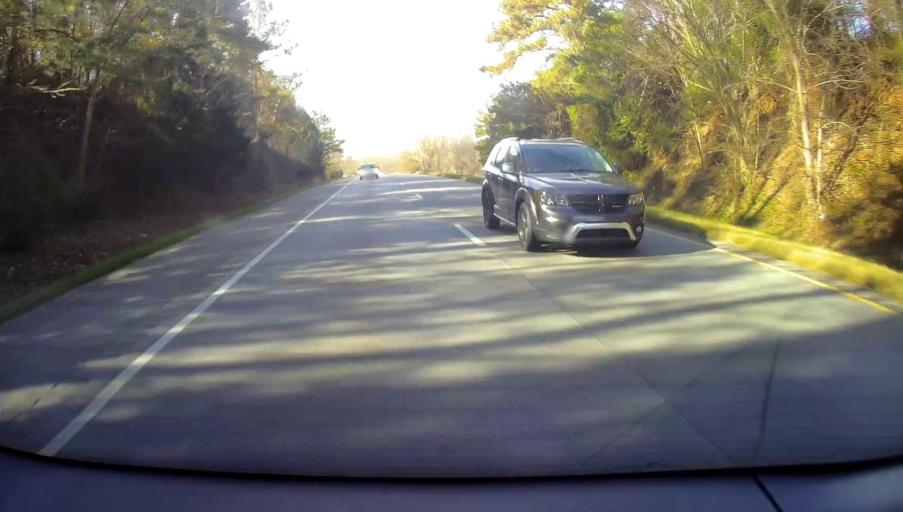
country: US
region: Alabama
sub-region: Colbert County
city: Tuscumbia
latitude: 34.7138
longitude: -87.7793
